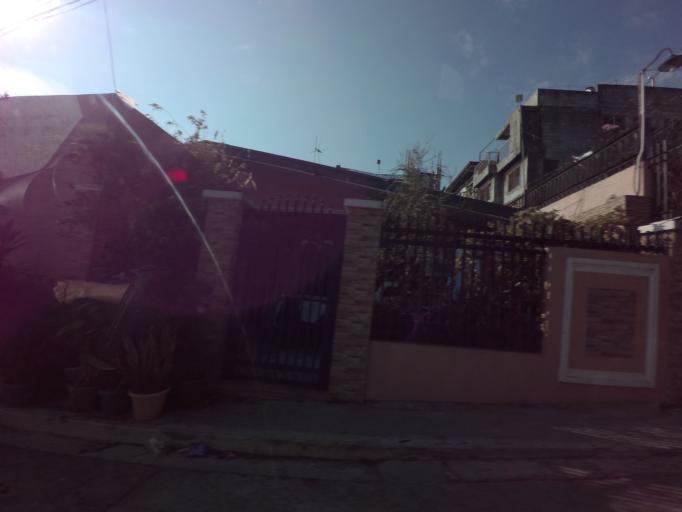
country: PH
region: Calabarzon
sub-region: Province of Rizal
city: Taguig
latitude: 14.4985
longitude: 121.0515
